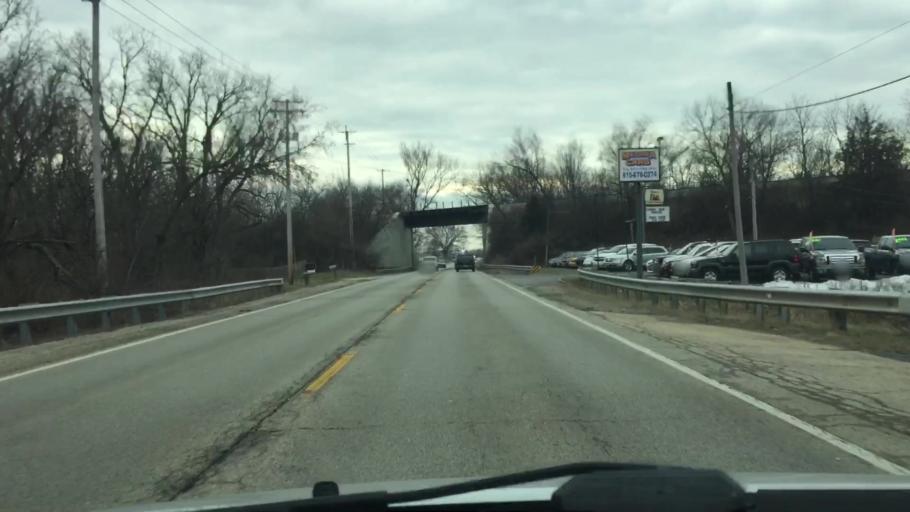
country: US
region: Illinois
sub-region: McHenry County
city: Richmond
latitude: 42.4574
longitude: -88.3060
